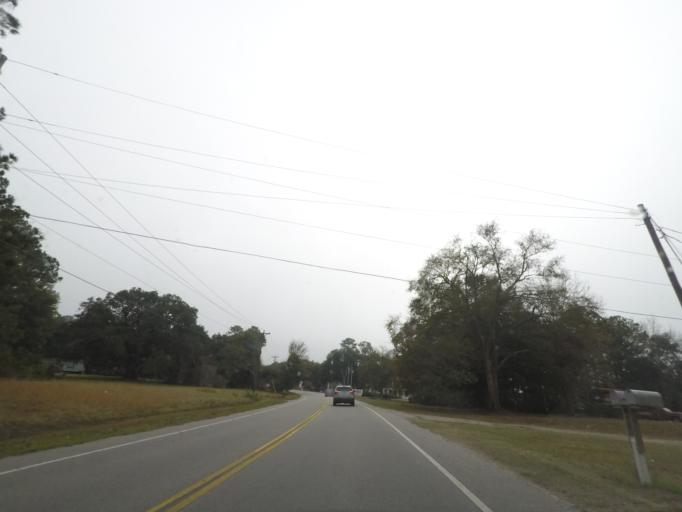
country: US
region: South Carolina
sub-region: Charleston County
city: Seabrook Island
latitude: 32.5236
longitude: -80.2996
